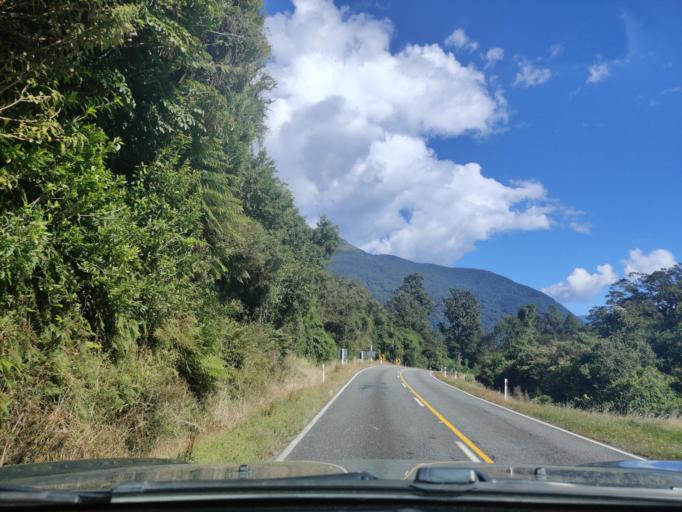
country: NZ
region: Otago
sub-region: Queenstown-Lakes District
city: Wanaka
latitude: -43.9706
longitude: 169.4074
